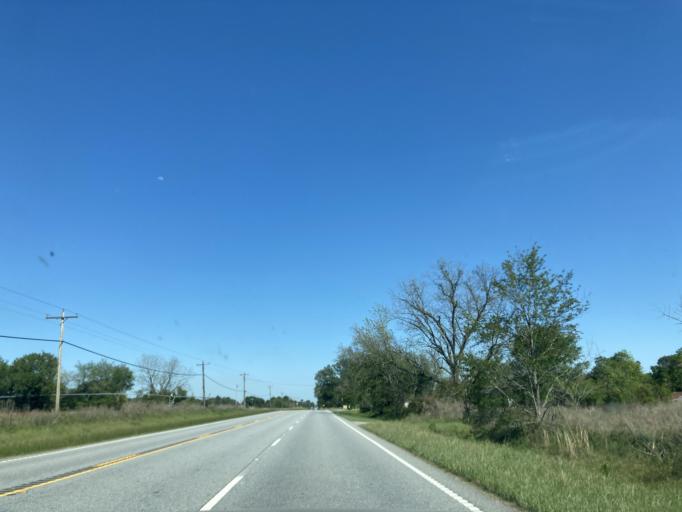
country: US
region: Georgia
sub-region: Miller County
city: Colquitt
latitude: 31.1851
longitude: -84.5952
